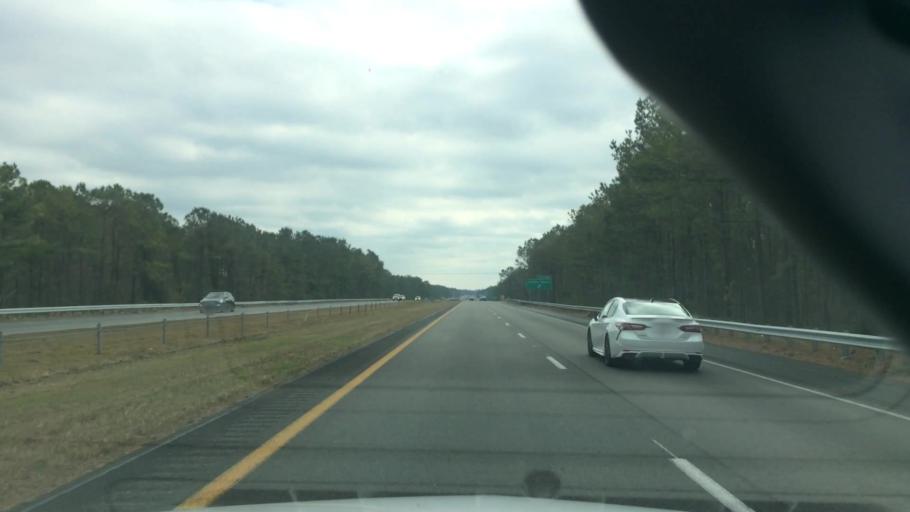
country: US
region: North Carolina
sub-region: New Hanover County
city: Castle Hayne
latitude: 34.3557
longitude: -77.8863
